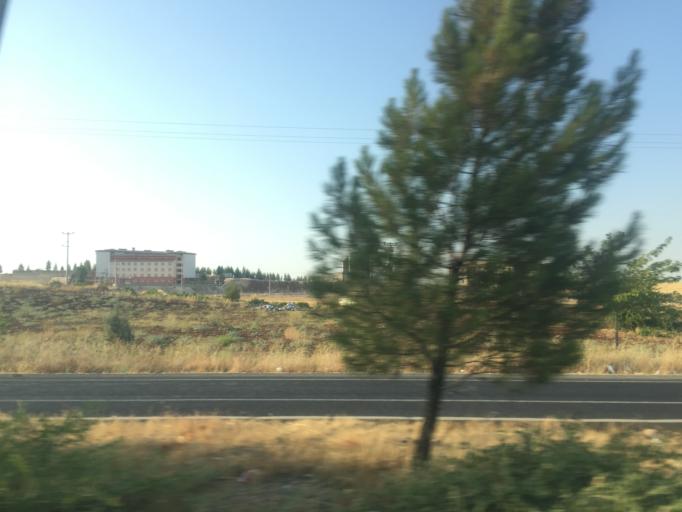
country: TR
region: Mardin
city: Acirli
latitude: 37.4374
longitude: 41.3073
